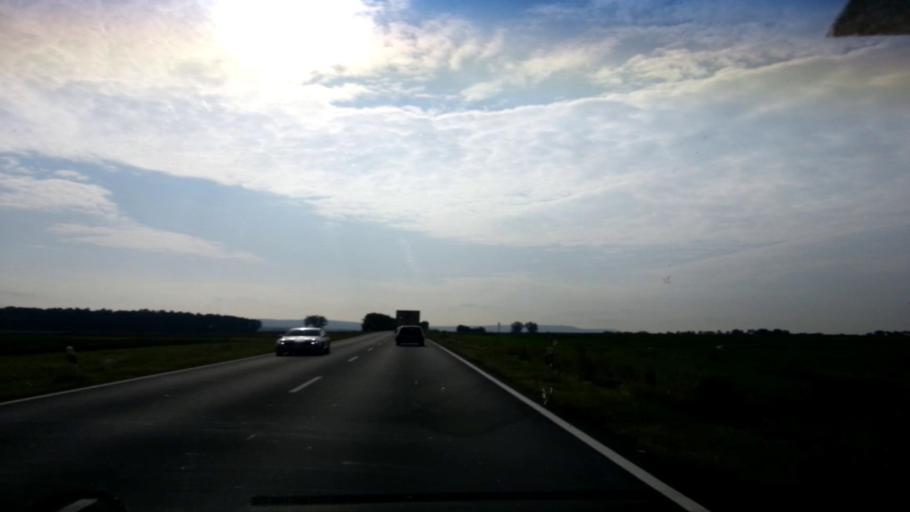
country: DE
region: Bavaria
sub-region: Regierungsbezirk Unterfranken
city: Prichsenstadt
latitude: 49.8285
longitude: 10.3557
